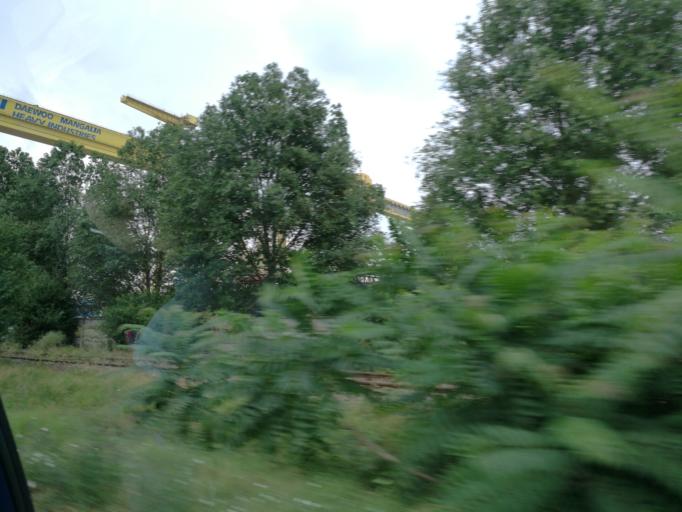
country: RO
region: Constanta
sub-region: Municipiul Mangalia
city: Mangalia
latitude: 43.7946
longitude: 28.5729
